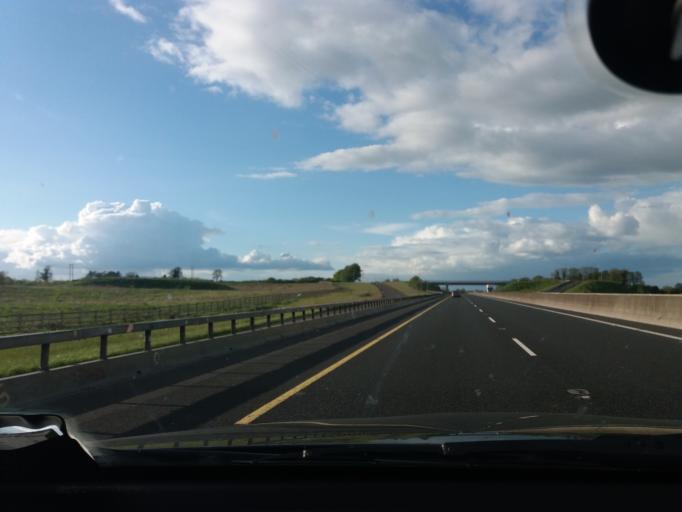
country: IE
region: Leinster
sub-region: Kildare
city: Old Kilcullen
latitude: 53.0865
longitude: -6.7537
